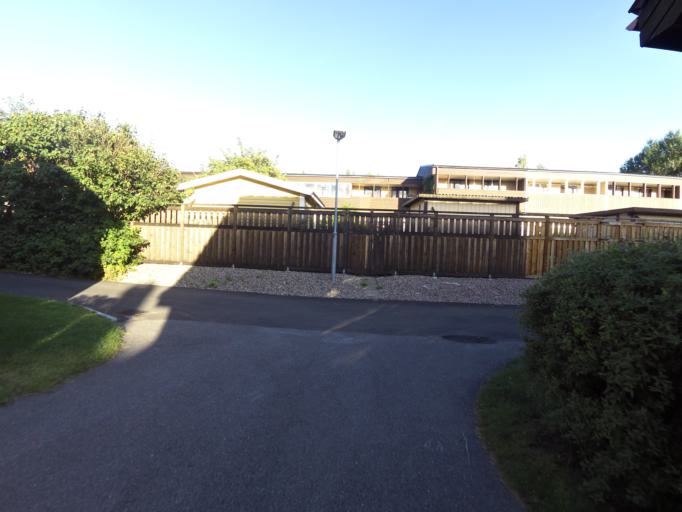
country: SE
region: Gaevleborg
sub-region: Gavle Kommun
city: Gavle
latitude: 60.7195
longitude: 17.1674
